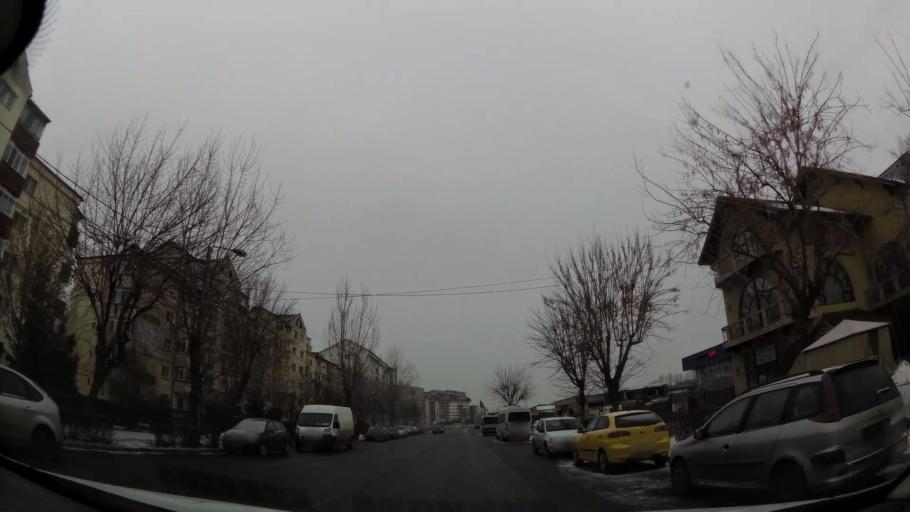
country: RO
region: Dambovita
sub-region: Municipiul Targoviste
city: Targoviste
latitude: 44.9306
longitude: 25.4387
